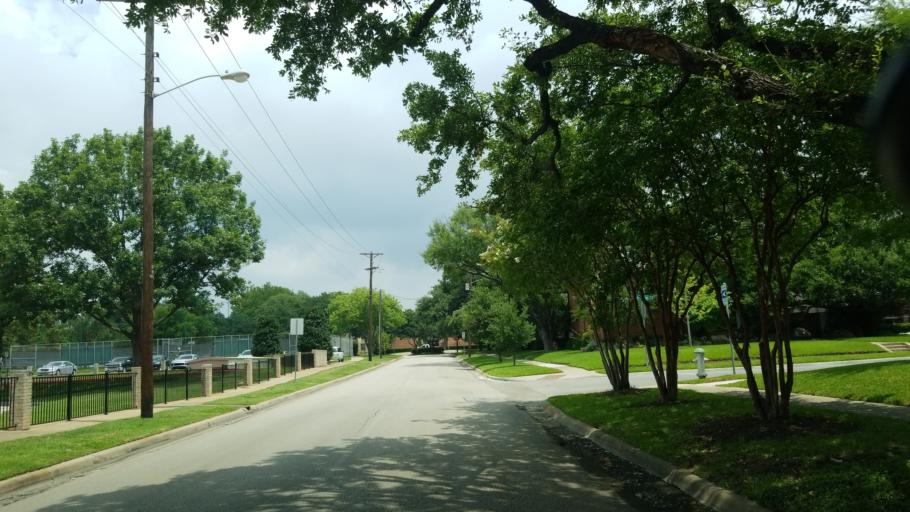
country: US
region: Texas
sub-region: Dallas County
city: University Park
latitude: 32.8441
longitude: -96.8129
